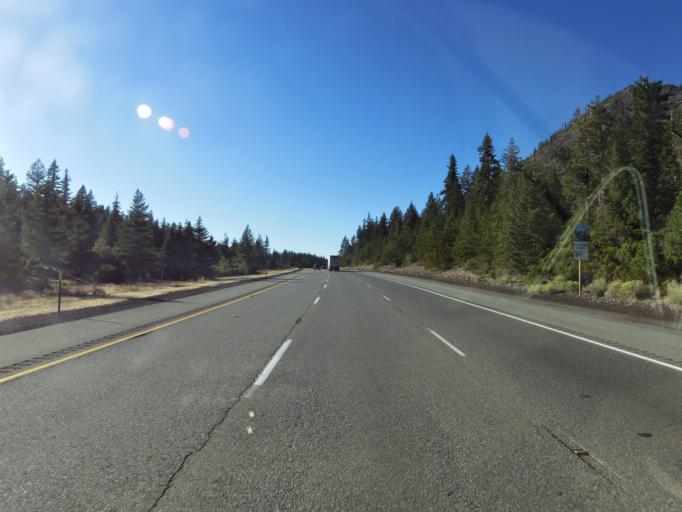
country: US
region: California
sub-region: Siskiyou County
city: Mount Shasta
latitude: 41.3525
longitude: -122.3520
